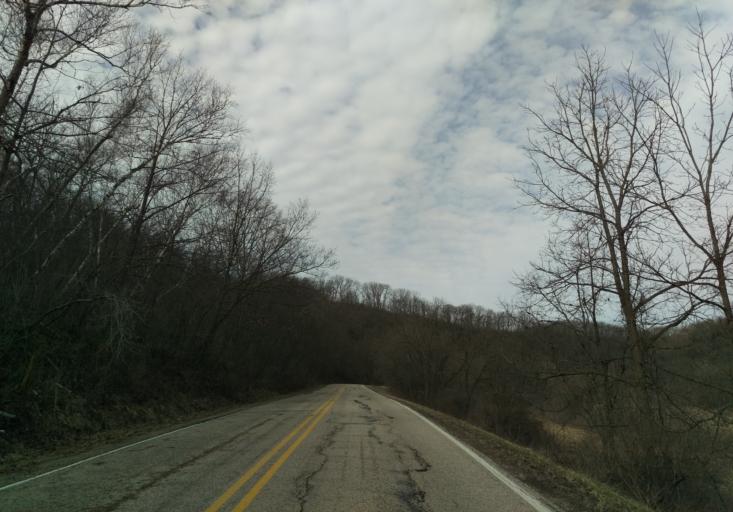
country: US
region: Wisconsin
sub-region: Dane County
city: Mount Horeb
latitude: 43.0622
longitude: -89.7907
